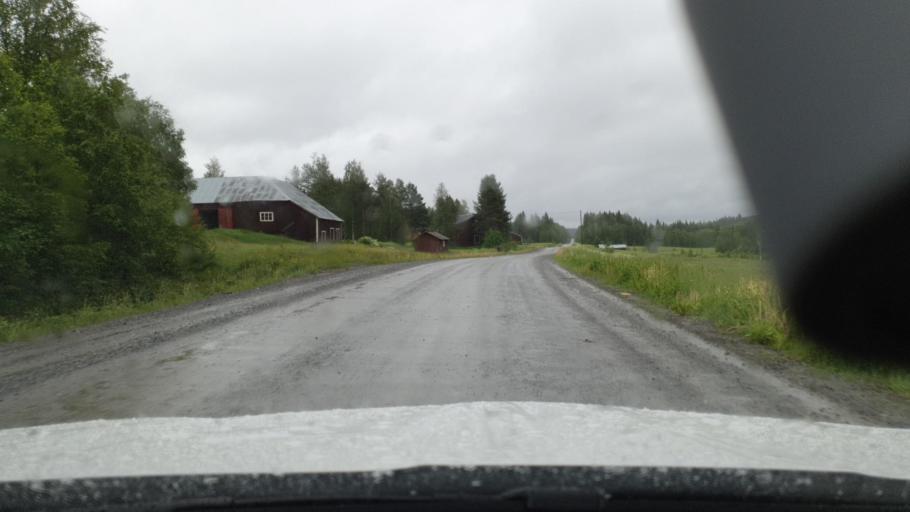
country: SE
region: Vaesterbotten
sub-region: Skelleftea Kommun
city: Burtraesk
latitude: 64.3846
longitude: 20.3106
